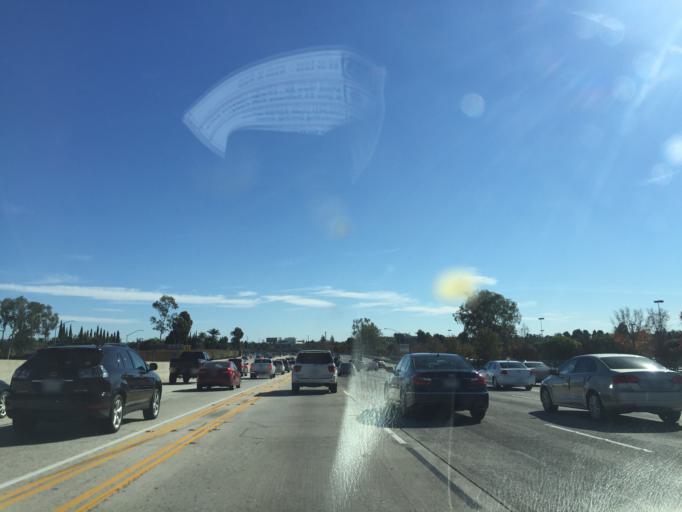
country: US
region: California
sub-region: Orange County
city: Laguna Hills
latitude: 33.6136
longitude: -117.7065
